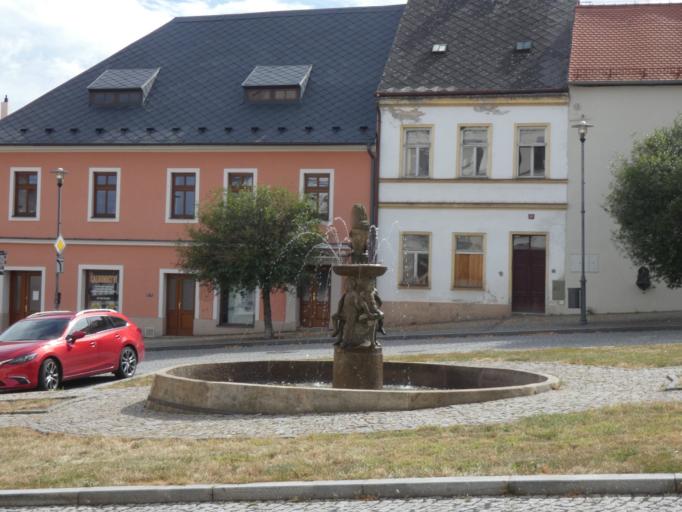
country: CZ
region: Ustecky
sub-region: Okres Chomutov
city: Klasterec nad Ohri
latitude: 50.3846
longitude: 13.1708
